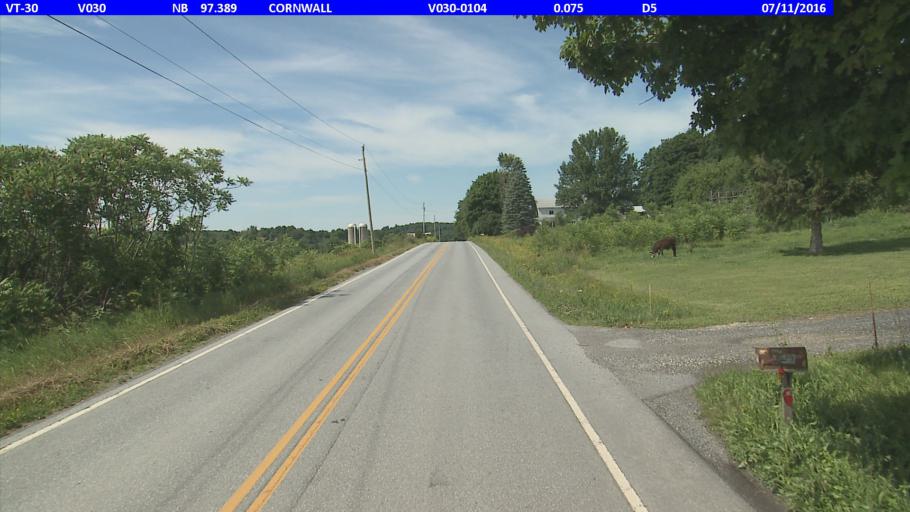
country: US
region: Vermont
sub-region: Addison County
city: Middlebury (village)
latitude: 43.9091
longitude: -73.2083
